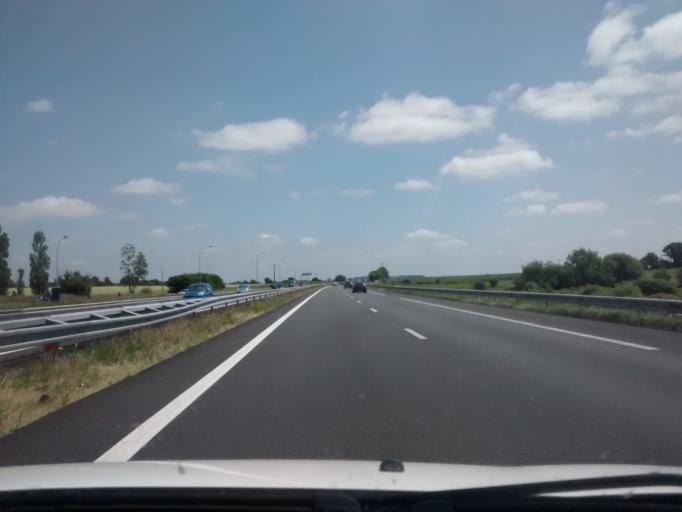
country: FR
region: Pays de la Loire
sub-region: Departement de la Mayenne
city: Sainte-Suzanne
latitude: 48.0229
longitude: -0.3253
